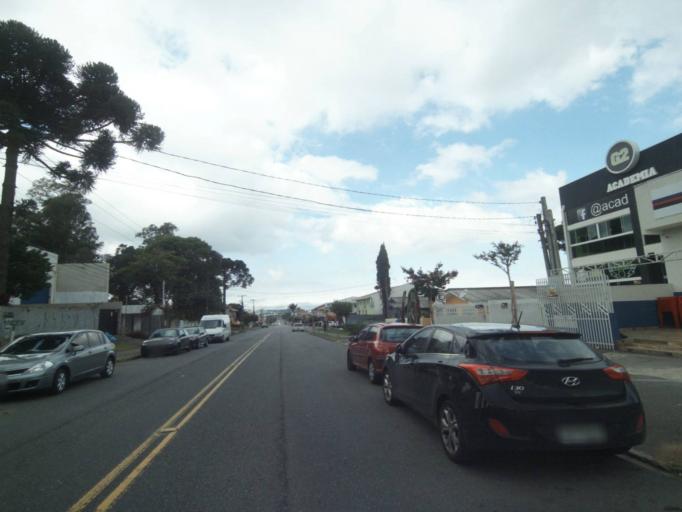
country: BR
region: Parana
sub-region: Pinhais
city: Pinhais
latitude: -25.4520
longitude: -49.2122
